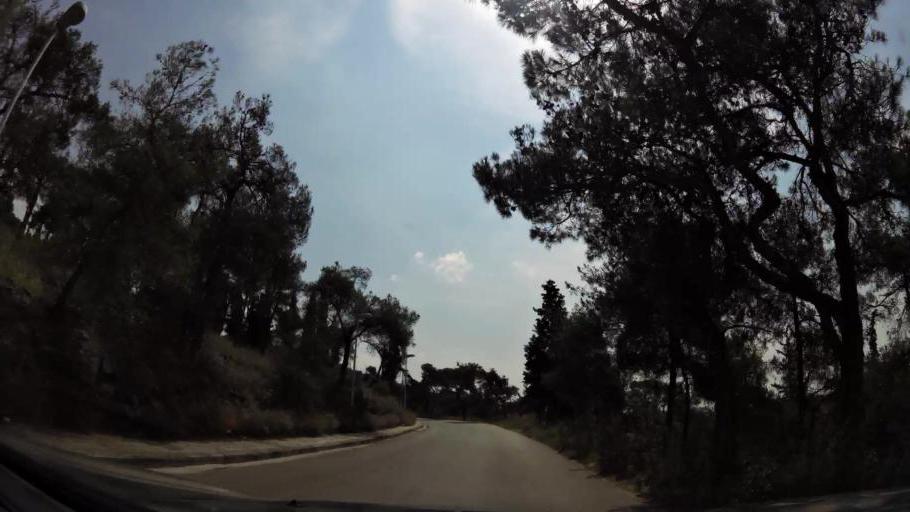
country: GR
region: Central Macedonia
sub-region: Nomos Thessalonikis
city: Agios Pavlos
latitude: 40.6349
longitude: 22.9665
